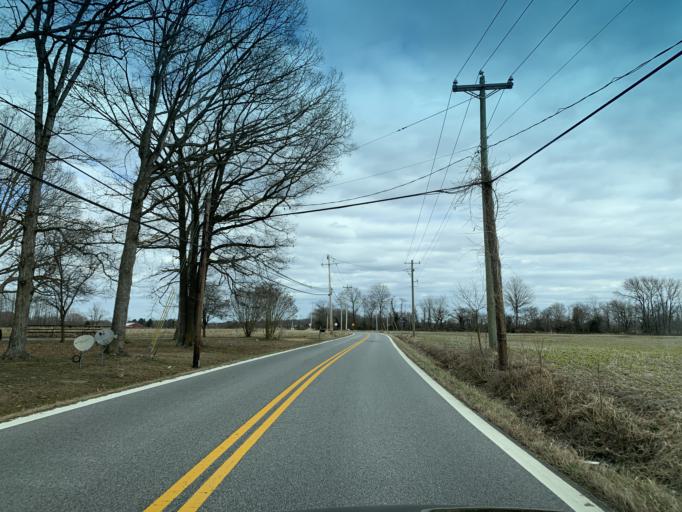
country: US
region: Maryland
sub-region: Queen Anne's County
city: Centreville
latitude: 39.0299
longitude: -76.0934
